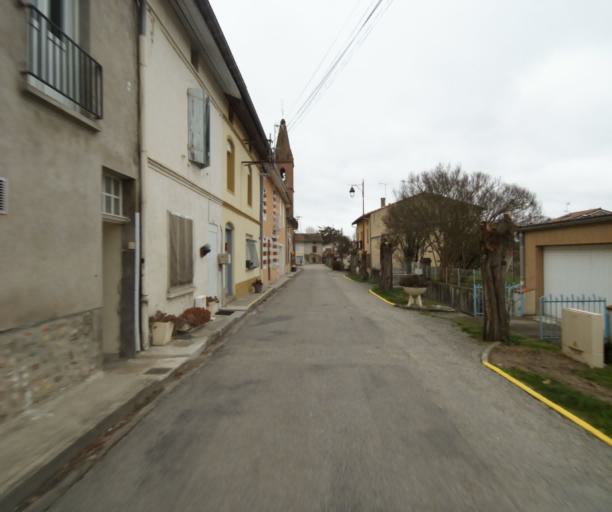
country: FR
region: Midi-Pyrenees
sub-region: Departement de l'Ariege
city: Saverdun
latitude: 43.1847
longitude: 1.6018
